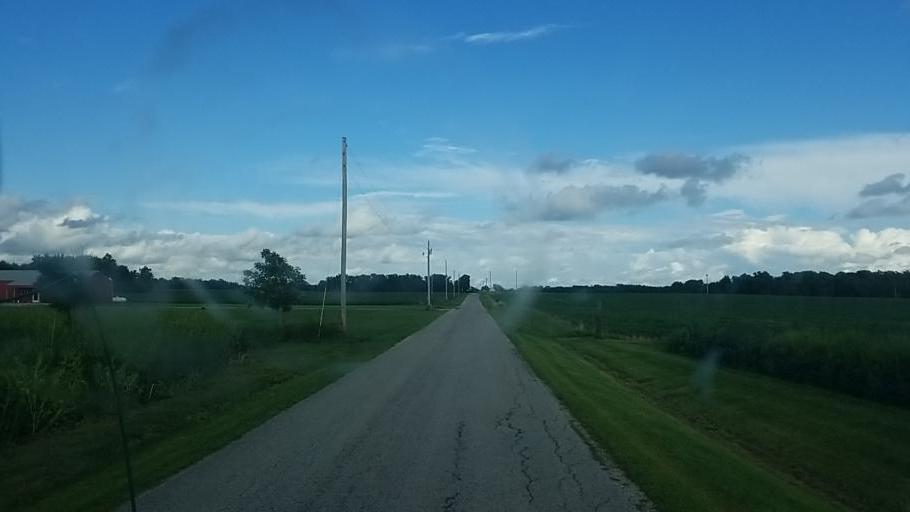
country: US
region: Ohio
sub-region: Hardin County
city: Forest
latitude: 40.7885
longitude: -83.4235
